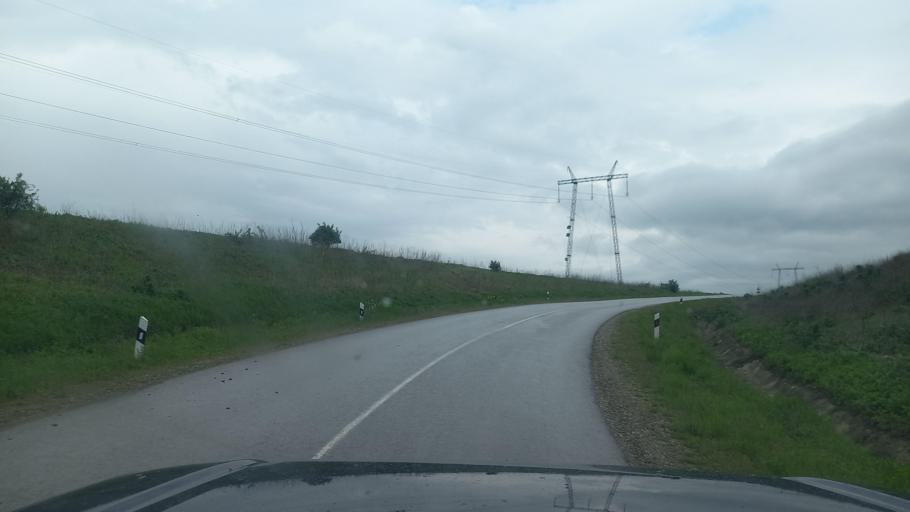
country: RU
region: Stavropol'skiy
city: Nevinnomyssk
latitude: 44.5896
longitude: 42.2290
